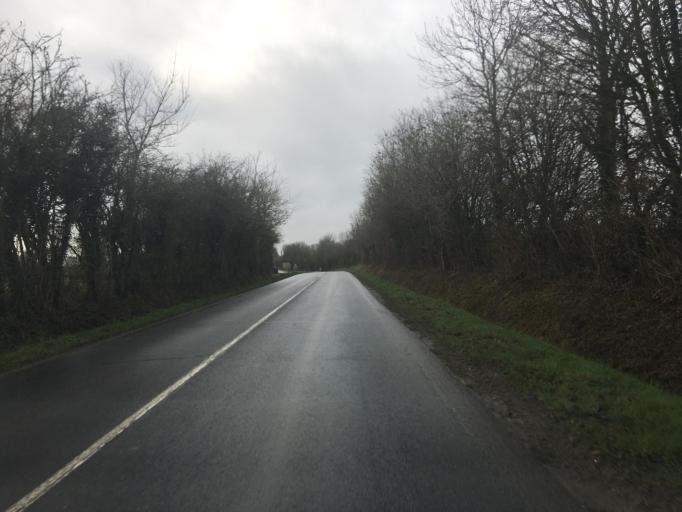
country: FR
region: Lower Normandy
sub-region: Departement du Calvados
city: Isigny-sur-Mer
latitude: 49.3553
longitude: -1.0744
